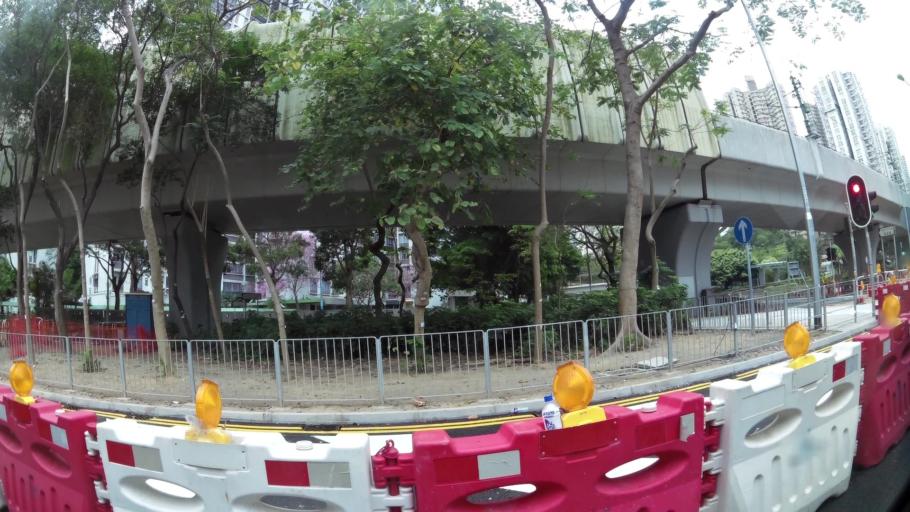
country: HK
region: Tsuen Wan
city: Tsuen Wan
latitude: 22.3608
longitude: 114.1312
